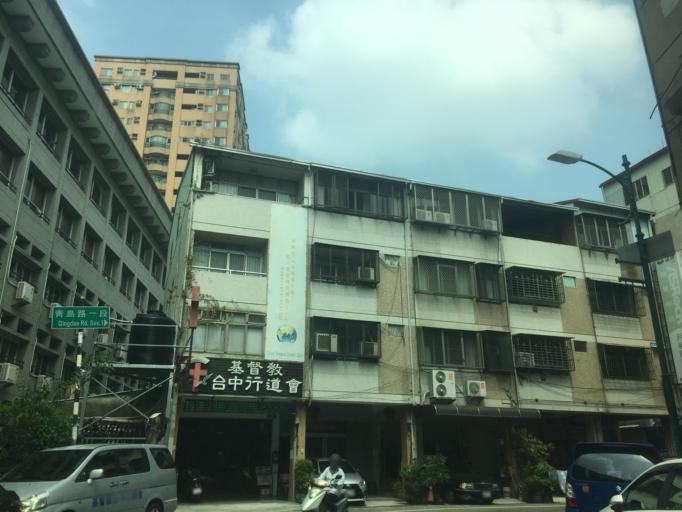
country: TW
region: Taiwan
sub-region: Taichung City
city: Taichung
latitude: 24.1688
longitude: 120.6745
